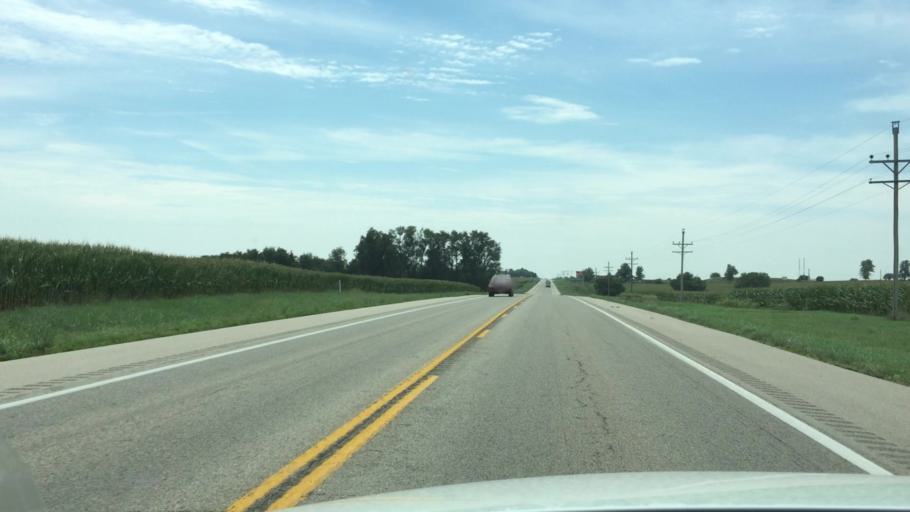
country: US
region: Kansas
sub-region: Nemaha County
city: Sabetha
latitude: 39.7650
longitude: -95.7296
